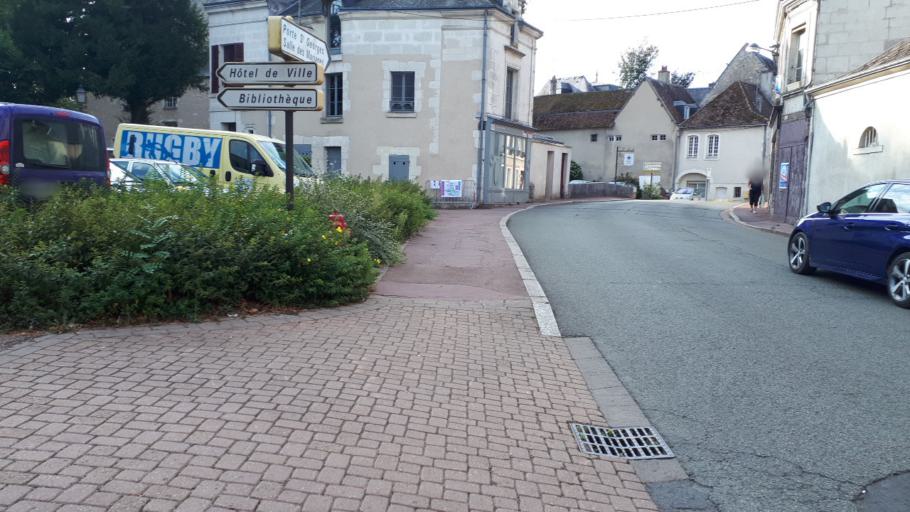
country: FR
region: Centre
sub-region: Departement du Loir-et-Cher
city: Vendome
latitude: 47.7936
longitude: 1.0648
